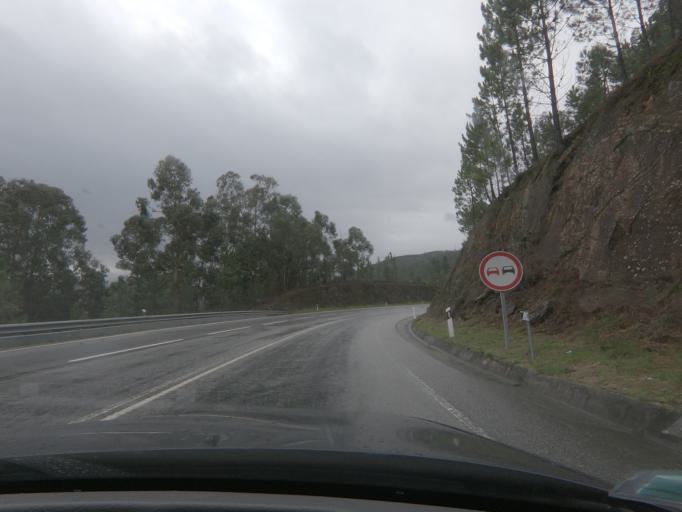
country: PT
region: Braga
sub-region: Celorico de Basto
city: Celorico de Basto
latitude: 41.3411
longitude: -8.0338
